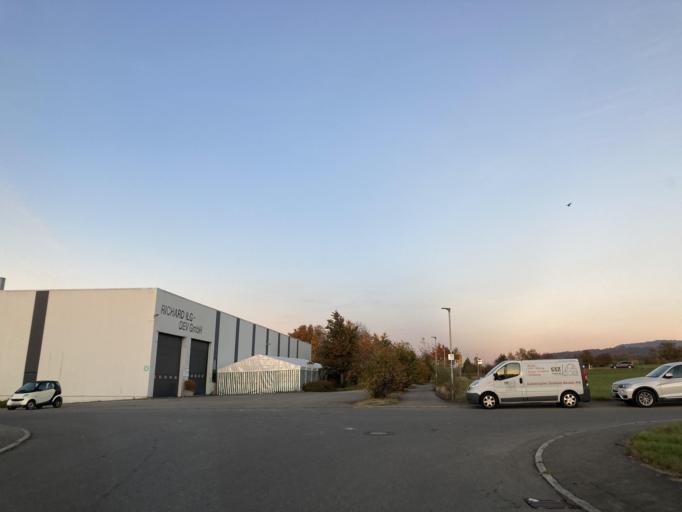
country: DE
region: Baden-Wuerttemberg
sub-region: Tuebingen Region
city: Mossingen
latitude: 48.4170
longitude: 9.0553
